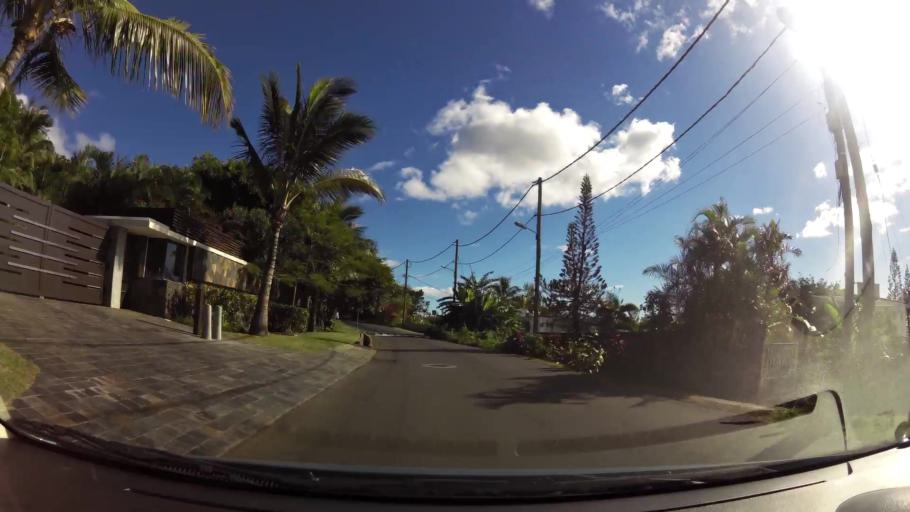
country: MU
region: Plaines Wilhems
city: Quatre Bornes
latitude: -20.2728
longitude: 57.4821
